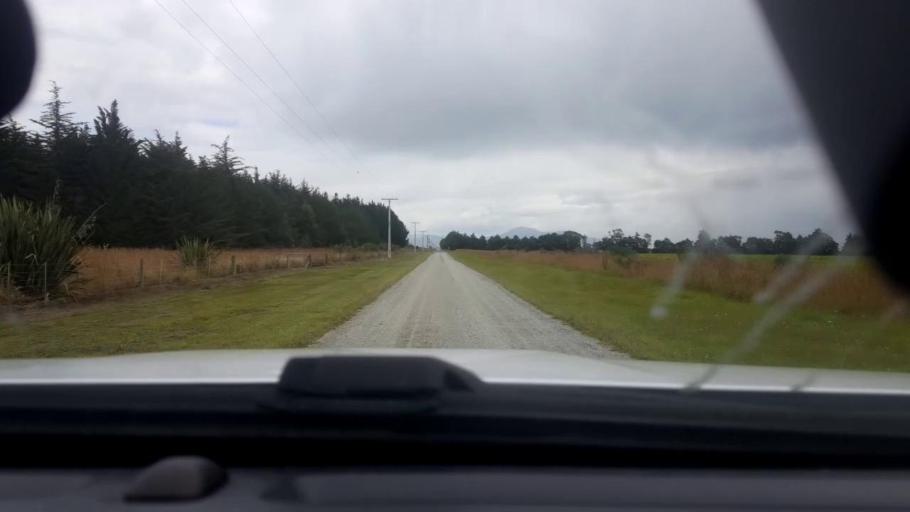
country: NZ
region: Canterbury
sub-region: Timaru District
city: Timaru
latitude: -44.1620
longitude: 171.4059
